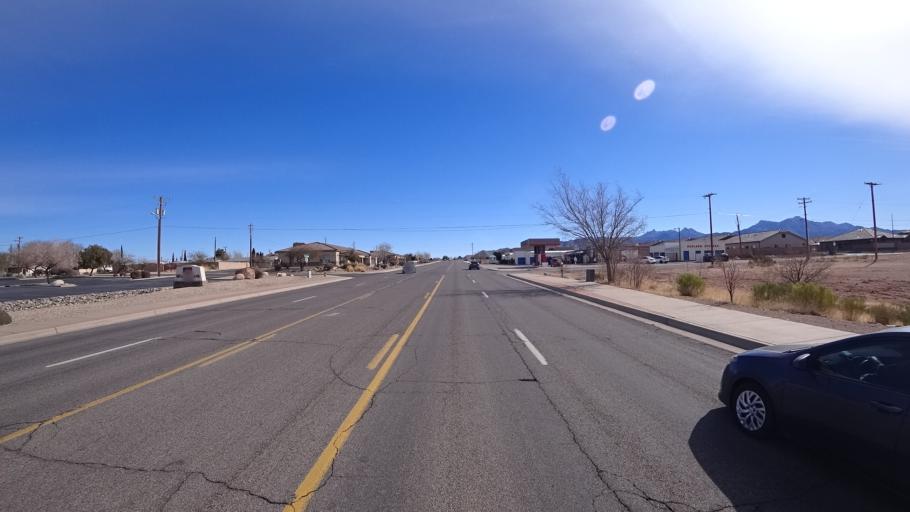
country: US
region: Arizona
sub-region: Mohave County
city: Kingman
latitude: 35.1913
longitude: -114.0209
